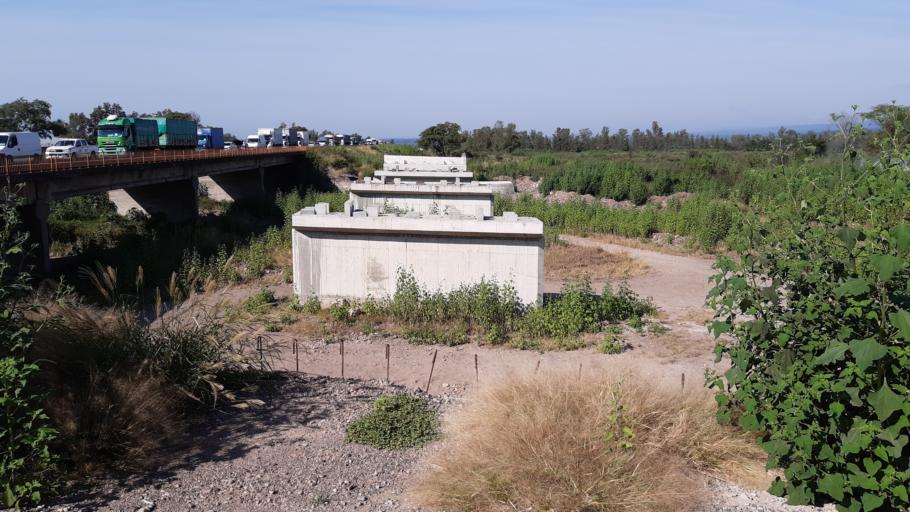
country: AR
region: Salta
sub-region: Departamento de General Guemes
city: General Martin Miguel de Guemes
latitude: -24.5616
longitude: -65.0791
